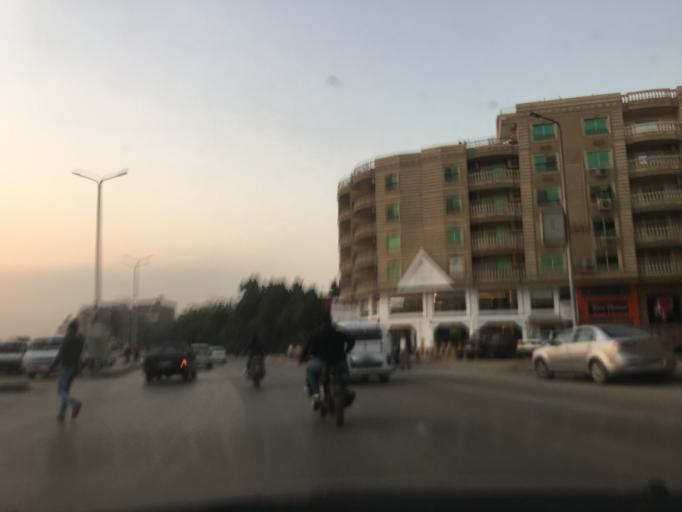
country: EG
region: Al Jizah
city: Al Jizah
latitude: 29.9883
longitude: 31.1402
